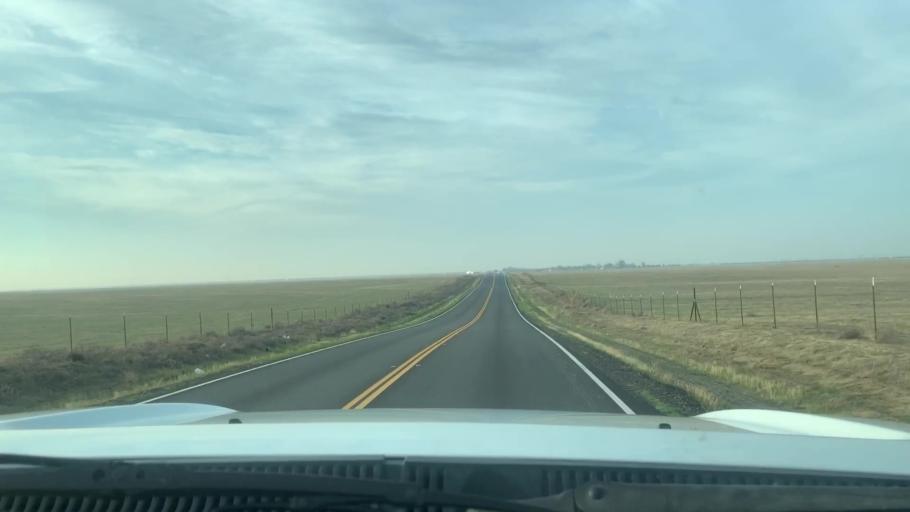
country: US
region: California
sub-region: Kern County
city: Lost Hills
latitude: 35.5961
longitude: -119.8446
